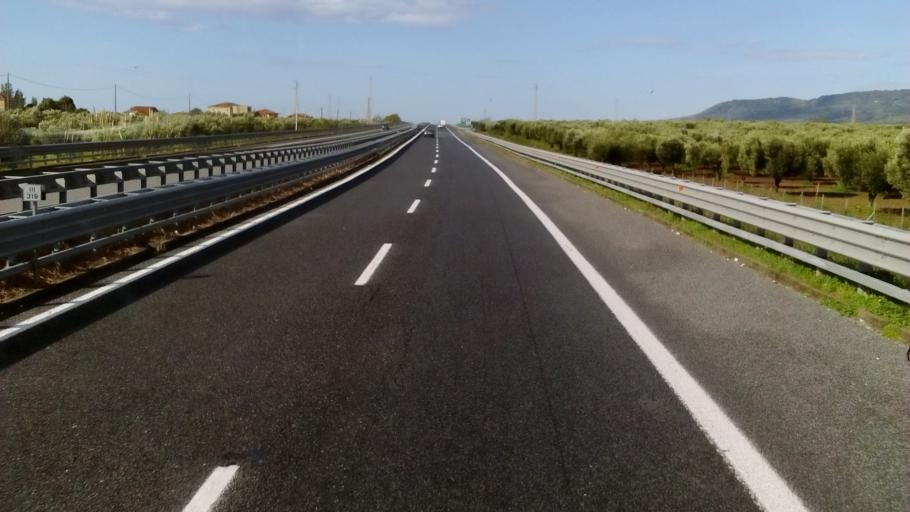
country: IT
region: Calabria
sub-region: Provincia di Catanzaro
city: Santa Eufemia Lamezia
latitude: 38.9240
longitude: 16.2579
